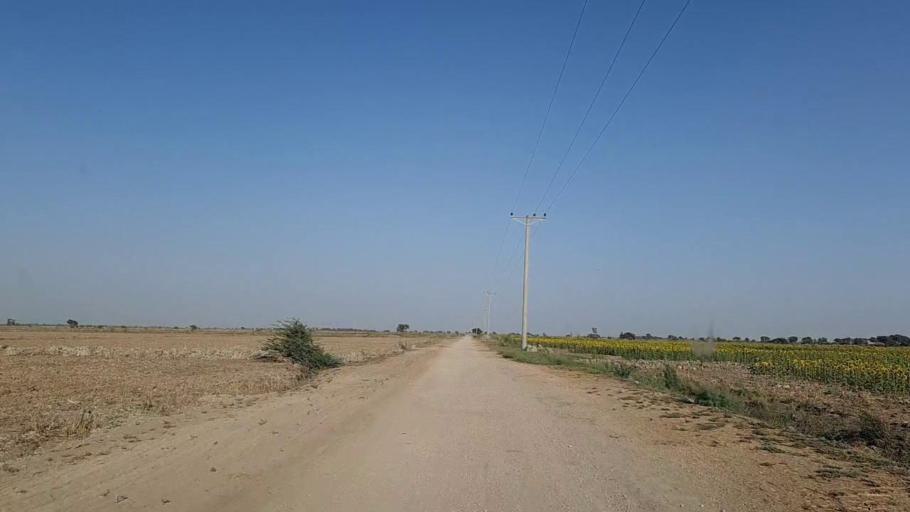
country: PK
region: Sindh
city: Jati
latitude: 24.4230
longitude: 68.2703
